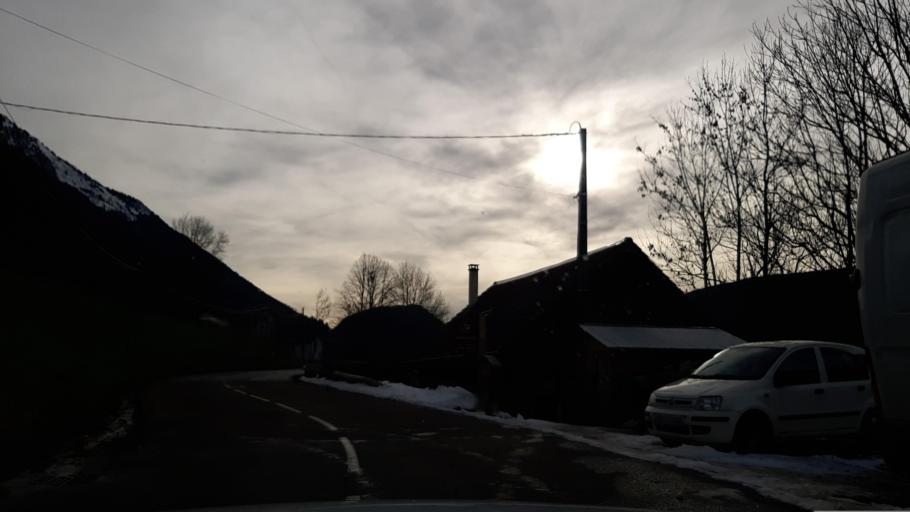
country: FR
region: Rhone-Alpes
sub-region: Departement de la Savoie
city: Cruet
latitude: 45.6550
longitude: 6.0944
